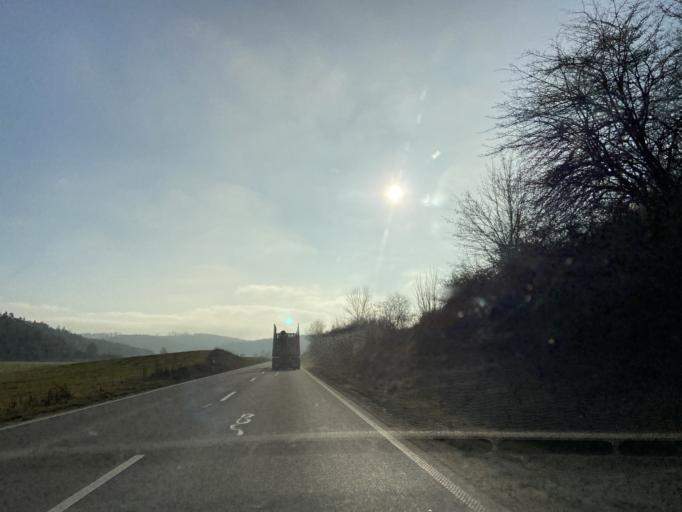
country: DE
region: Baden-Wuerttemberg
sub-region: Tuebingen Region
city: Sigmaringen
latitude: 48.1311
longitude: 9.2148
